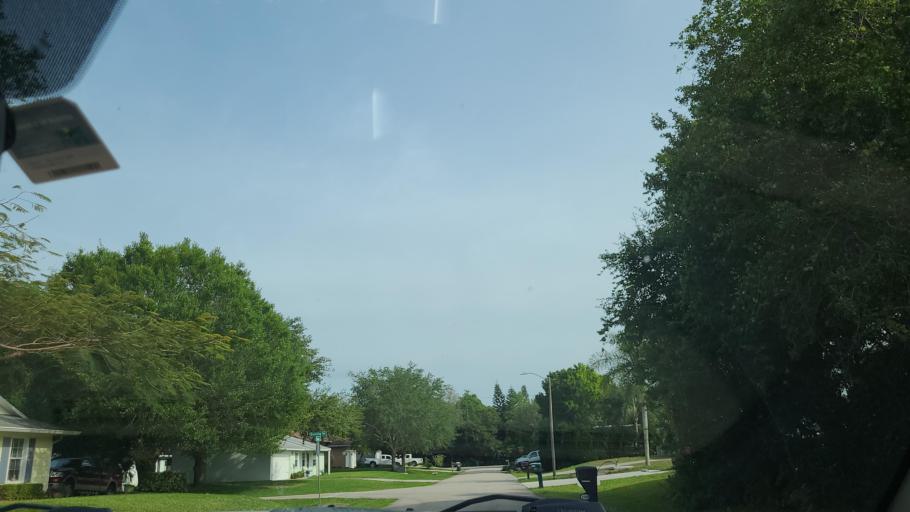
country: US
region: Florida
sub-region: Indian River County
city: Sebastian
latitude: 27.7656
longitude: -80.4891
